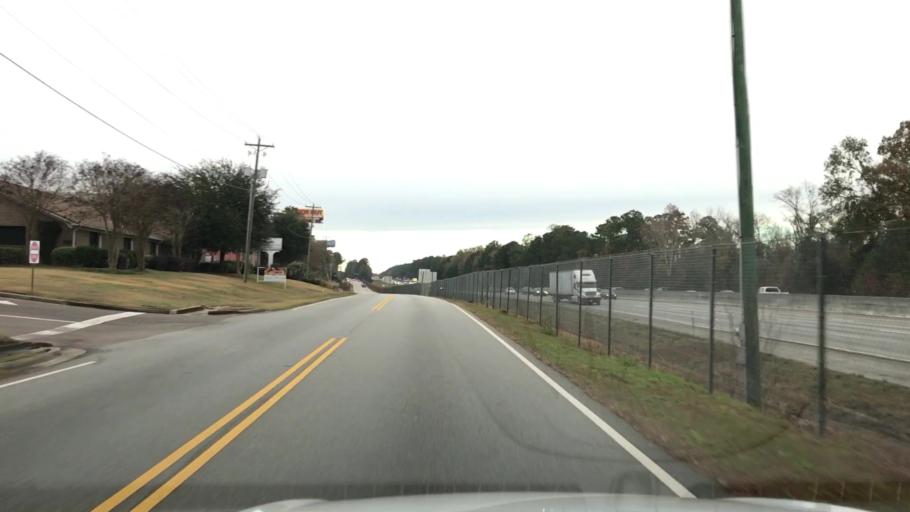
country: US
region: South Carolina
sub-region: Berkeley County
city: Hanahan
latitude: 32.9436
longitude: -80.0535
